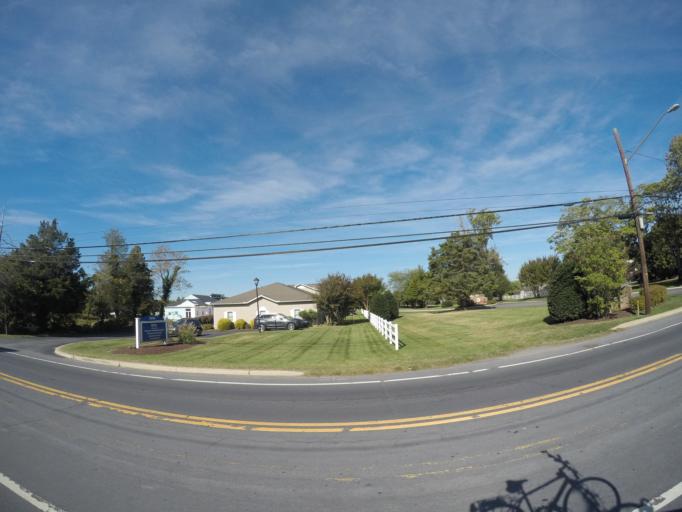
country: US
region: Delaware
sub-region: Sussex County
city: Lewes
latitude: 38.7534
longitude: -75.1616
